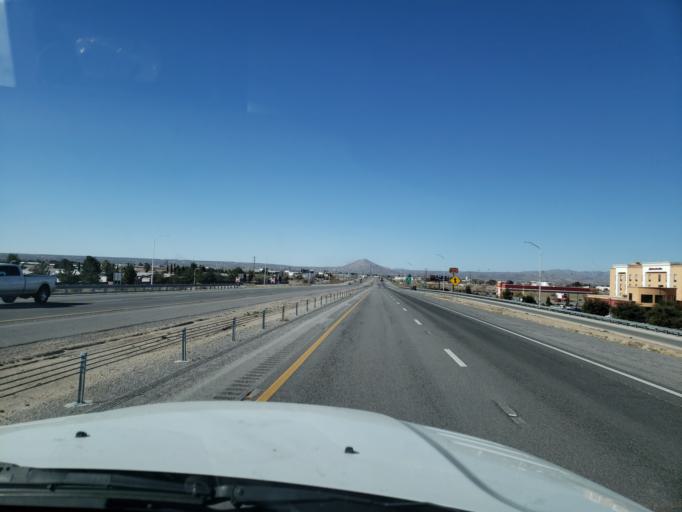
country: US
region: New Mexico
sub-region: Dona Ana County
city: Mesilla
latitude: 32.2906
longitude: -106.7922
